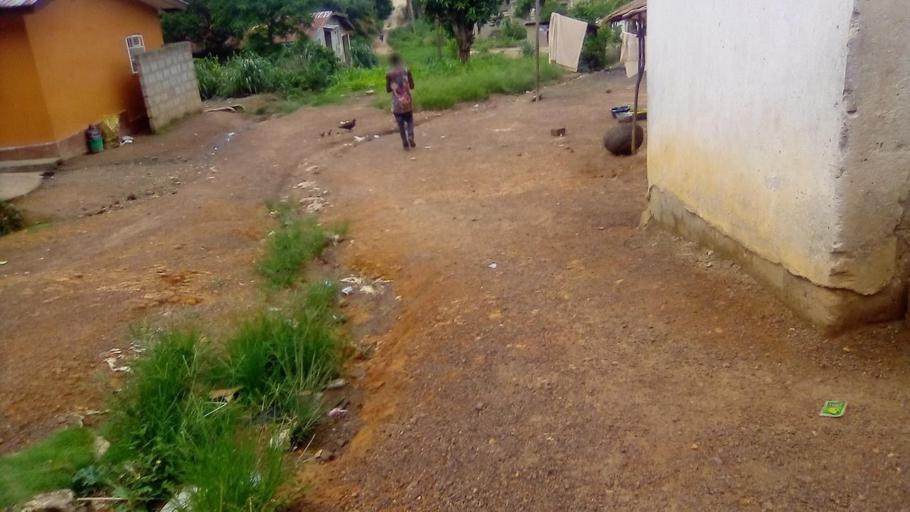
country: SL
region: Southern Province
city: Bo
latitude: 7.9422
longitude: -11.7412
